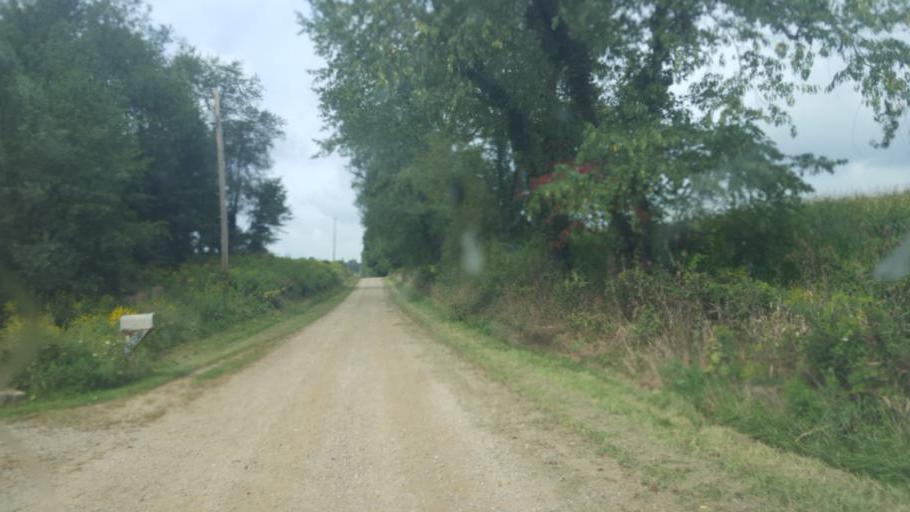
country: US
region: Ohio
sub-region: Knox County
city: Danville
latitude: 40.4758
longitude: -82.3490
